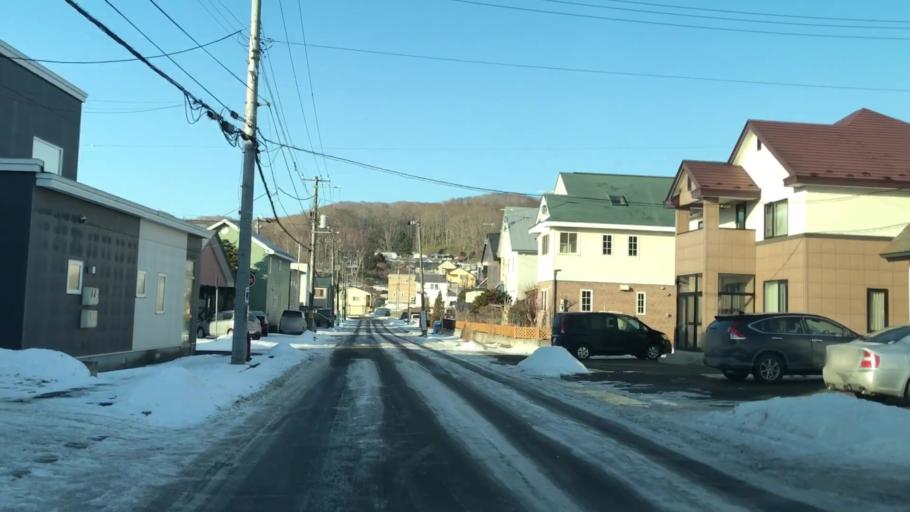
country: JP
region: Hokkaido
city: Muroran
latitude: 42.3893
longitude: 141.0680
